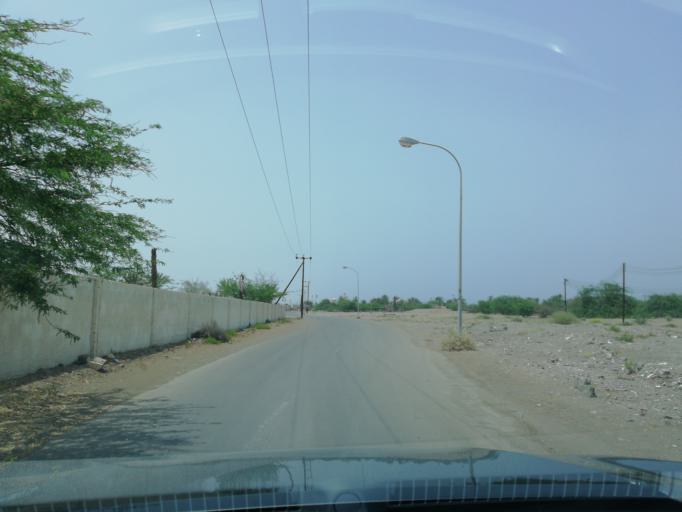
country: OM
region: Al Batinah
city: Al Liwa'
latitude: 24.6127
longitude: 56.5370
